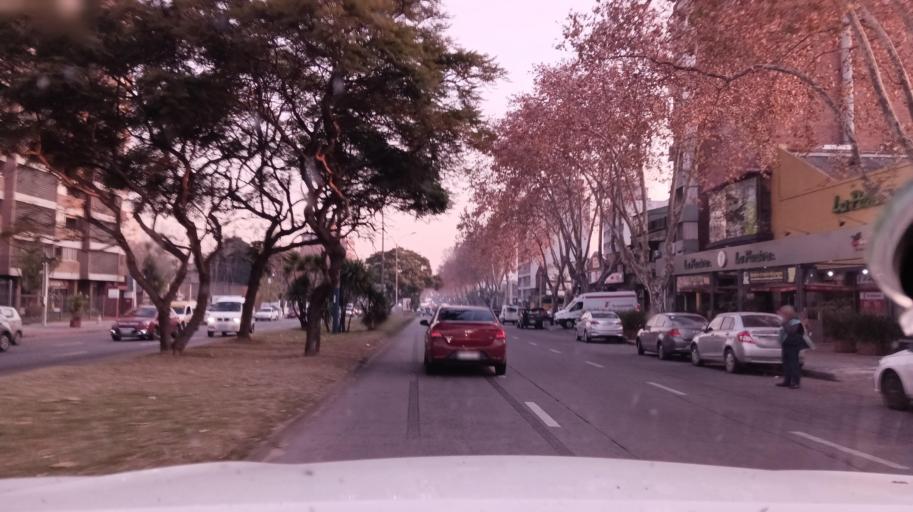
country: UY
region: Montevideo
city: Montevideo
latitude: -34.8673
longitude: -56.1721
